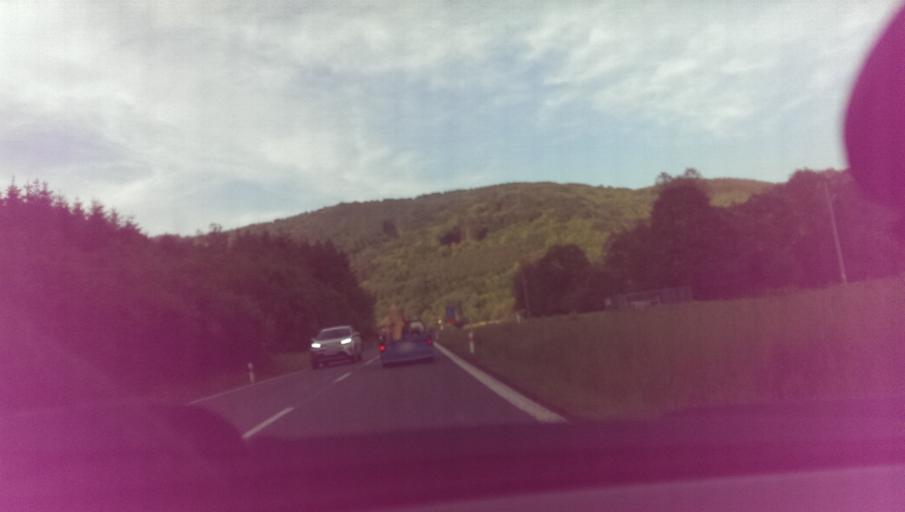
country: CZ
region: Zlin
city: Valasska Polanka
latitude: 49.2482
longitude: 17.9973
